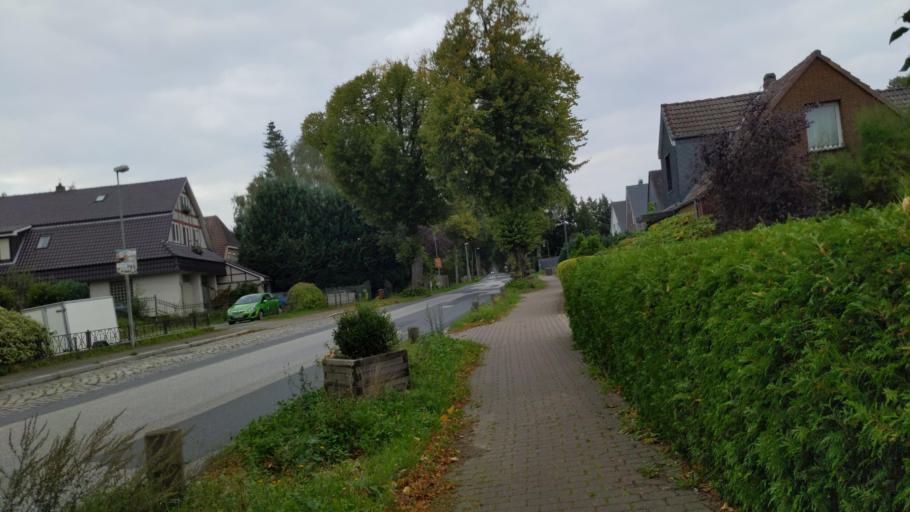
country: DE
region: Schleswig-Holstein
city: Krummesse
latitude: 53.7875
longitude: 10.6406
